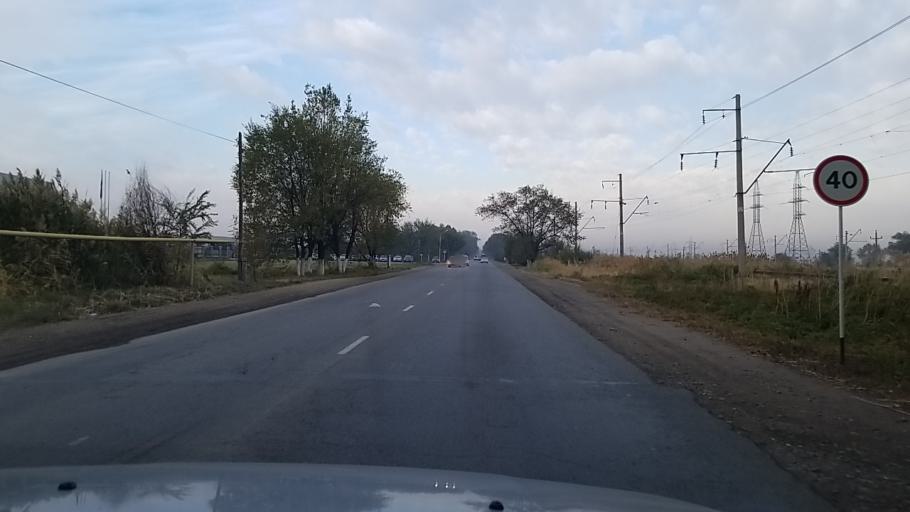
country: KZ
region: Almaty Oblysy
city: Burunday
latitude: 43.3577
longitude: 76.7834
